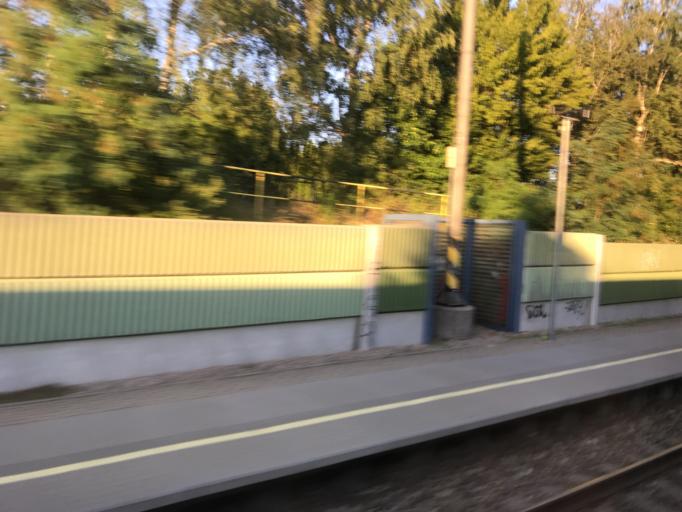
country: CZ
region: Central Bohemia
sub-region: Okres Praha-Vychod
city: Mnichovice
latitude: 49.9101
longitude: 14.7202
